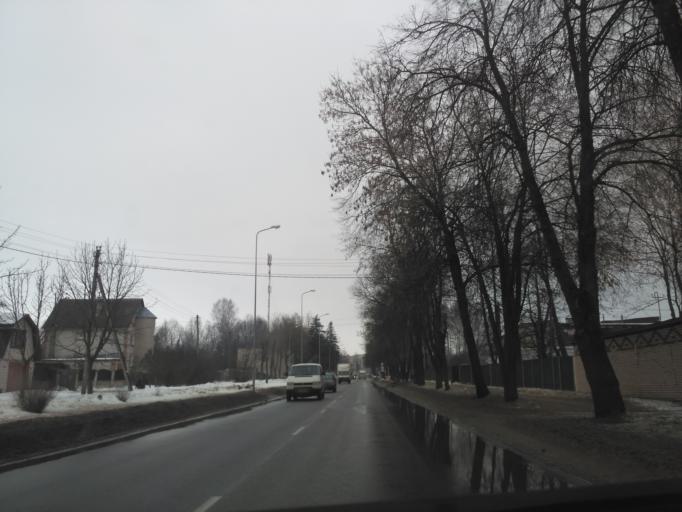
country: BY
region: Minsk
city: Horad Zhodzina
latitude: 54.0956
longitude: 28.3357
